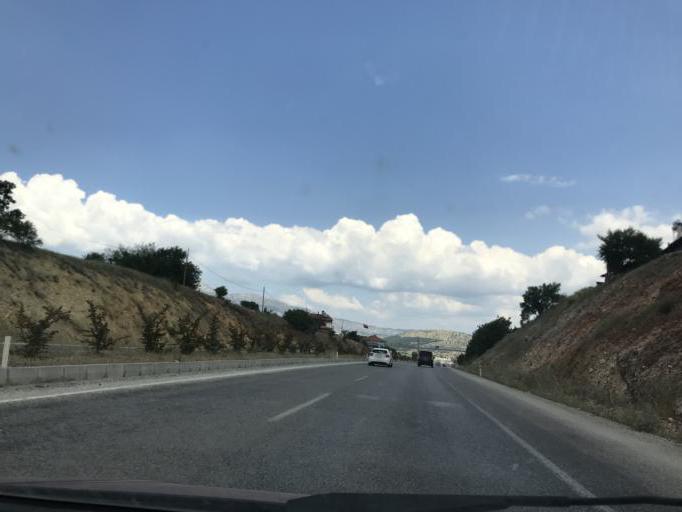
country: TR
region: Denizli
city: Serinhisar
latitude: 37.6157
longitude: 29.1682
